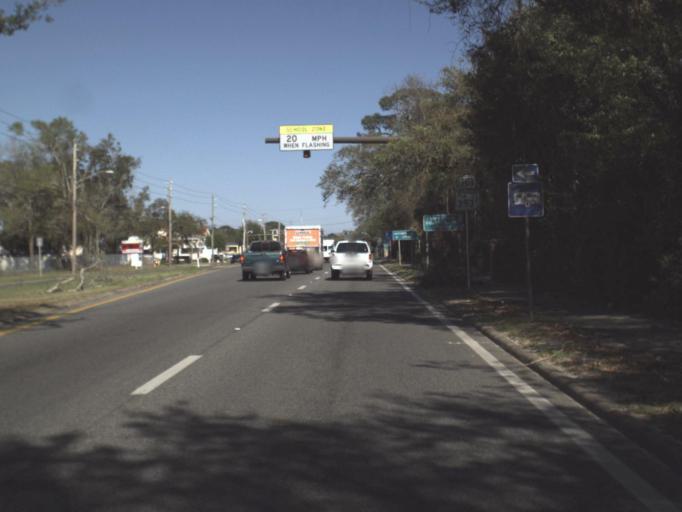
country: US
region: Florida
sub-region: Okaloosa County
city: Mary Esther
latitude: 30.4094
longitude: -86.6582
